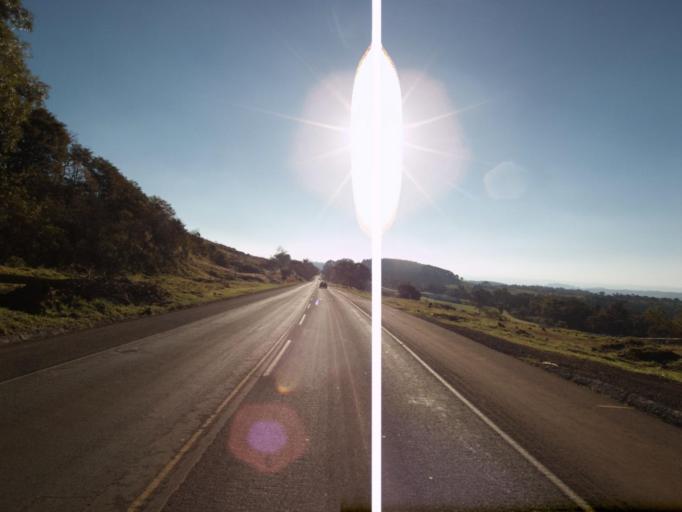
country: BR
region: Santa Catarina
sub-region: Chapeco
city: Chapeco
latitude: -26.9776
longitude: -52.7385
